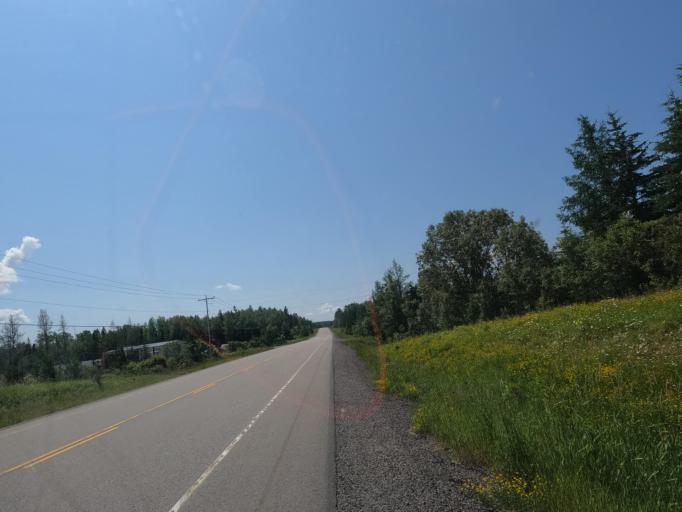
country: CA
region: Ontario
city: Dryden
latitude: 49.8789
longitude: -93.3592
